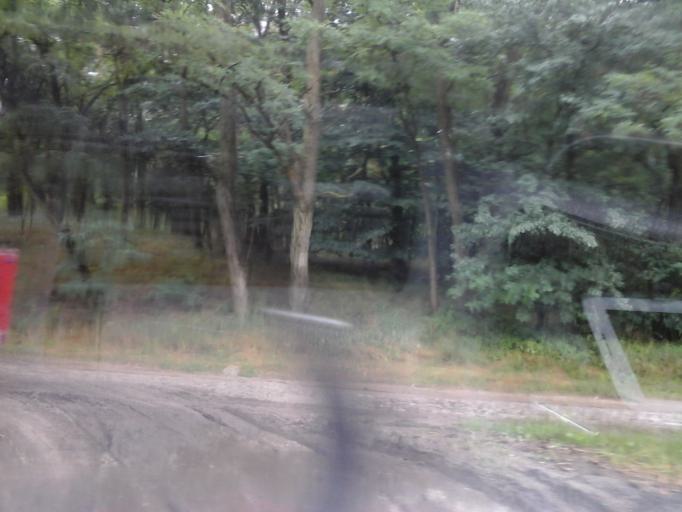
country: PL
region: West Pomeranian Voivodeship
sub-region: Powiat choszczenski
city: Bierzwnik
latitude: 52.9736
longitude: 15.6008
